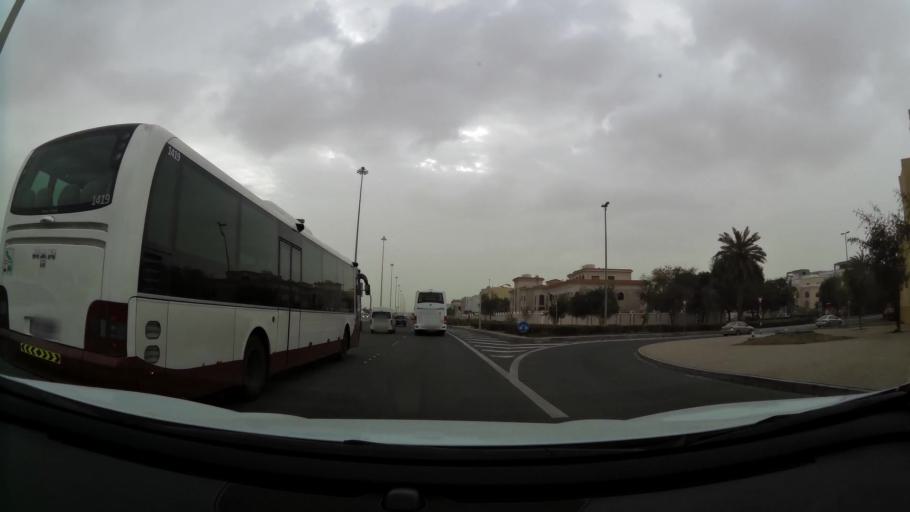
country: AE
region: Abu Dhabi
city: Abu Dhabi
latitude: 24.4479
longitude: 54.4099
